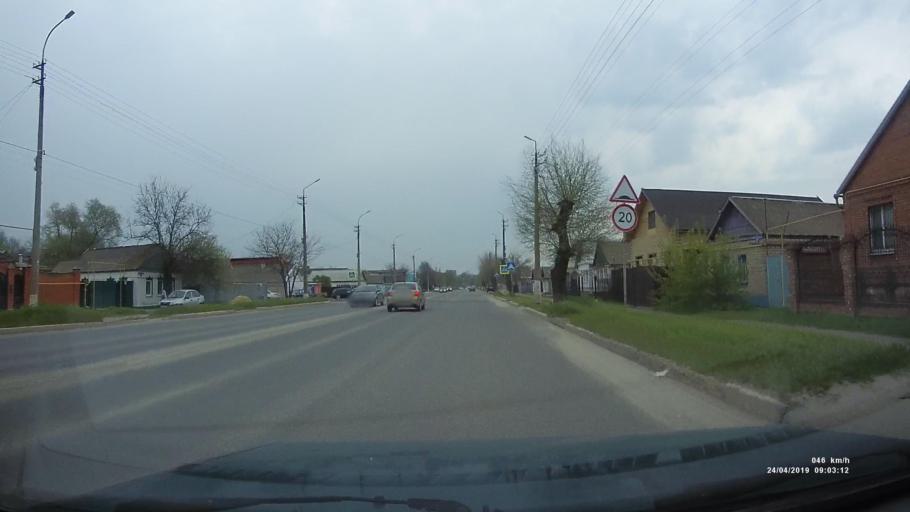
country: RU
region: Kalmykiya
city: Elista
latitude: 46.3115
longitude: 44.2365
